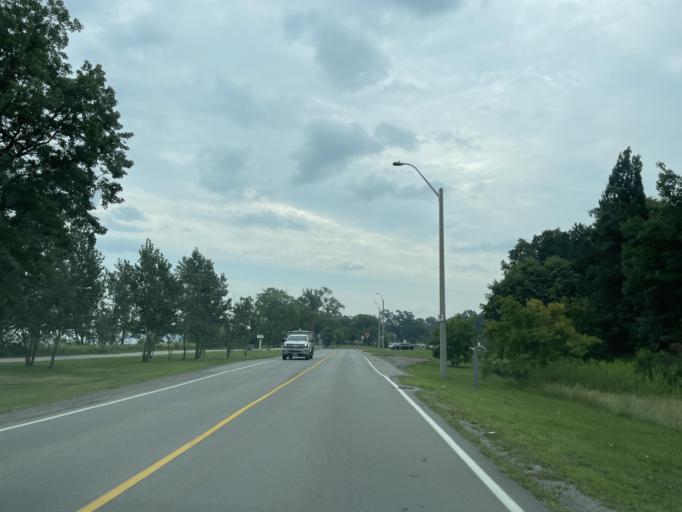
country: CA
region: Ontario
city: Hamilton
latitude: 43.2542
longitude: -79.7602
